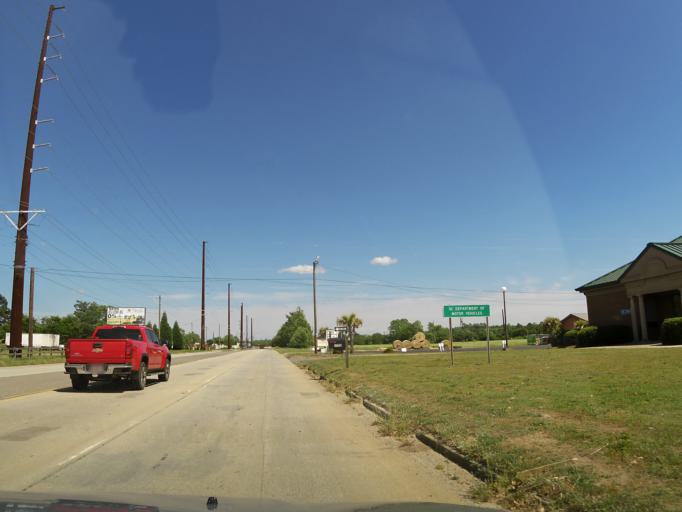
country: US
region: South Carolina
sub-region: Aiken County
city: Aiken
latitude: 33.5523
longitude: -81.6946
